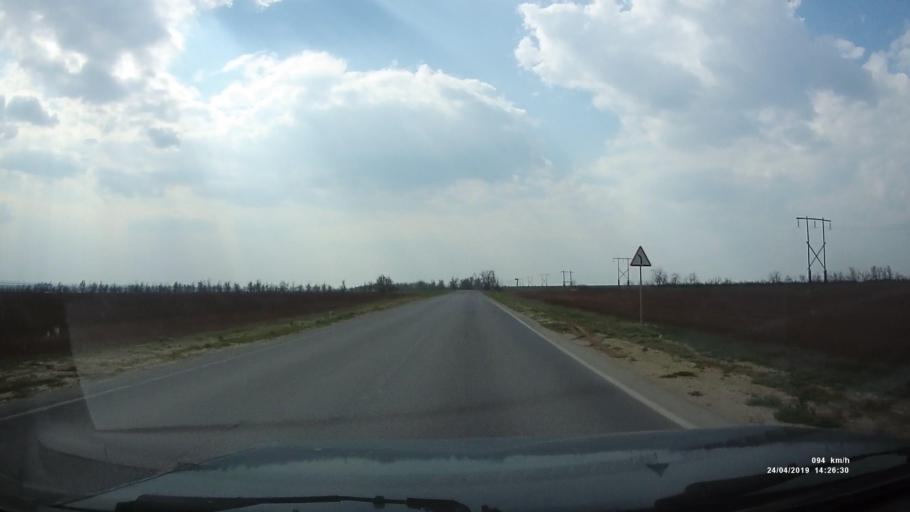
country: RU
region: Kalmykiya
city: Arshan'
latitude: 46.3335
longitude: 44.0630
